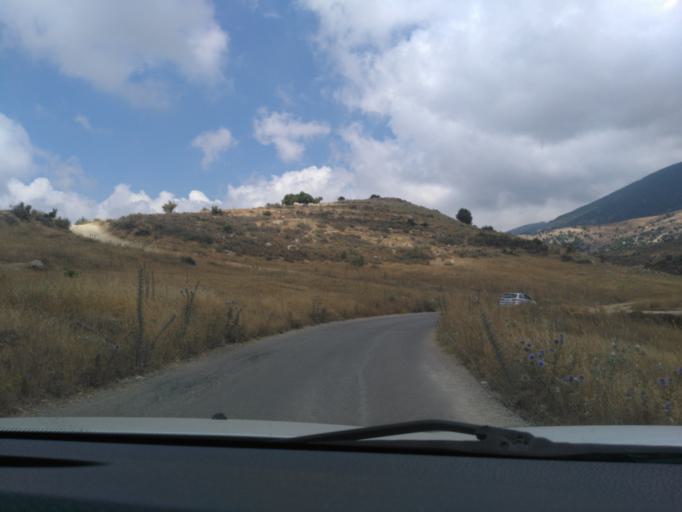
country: LB
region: Mont-Liban
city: Beit ed Dine
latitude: 33.6837
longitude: 35.6649
